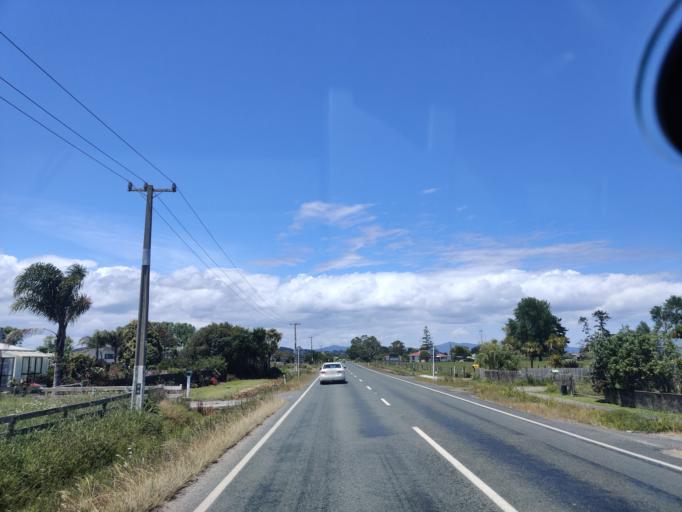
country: NZ
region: Northland
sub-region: Far North District
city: Kaitaia
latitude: -35.0402
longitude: 173.2556
